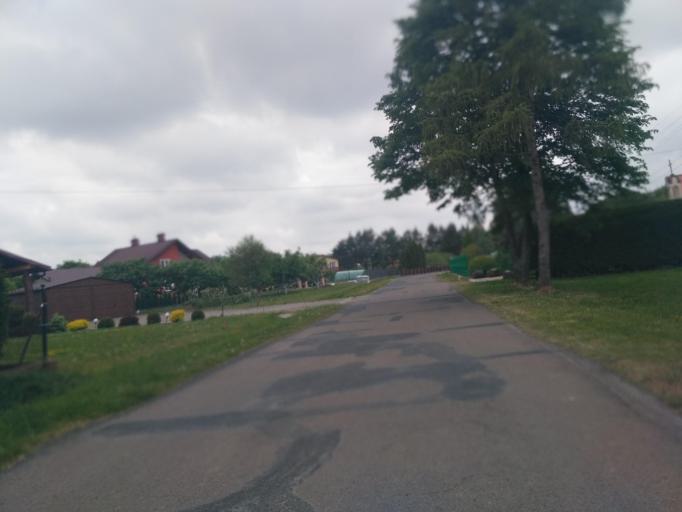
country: PL
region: Subcarpathian Voivodeship
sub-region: Powiat krosnienski
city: Chorkowka
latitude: 49.6680
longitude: 21.7014
